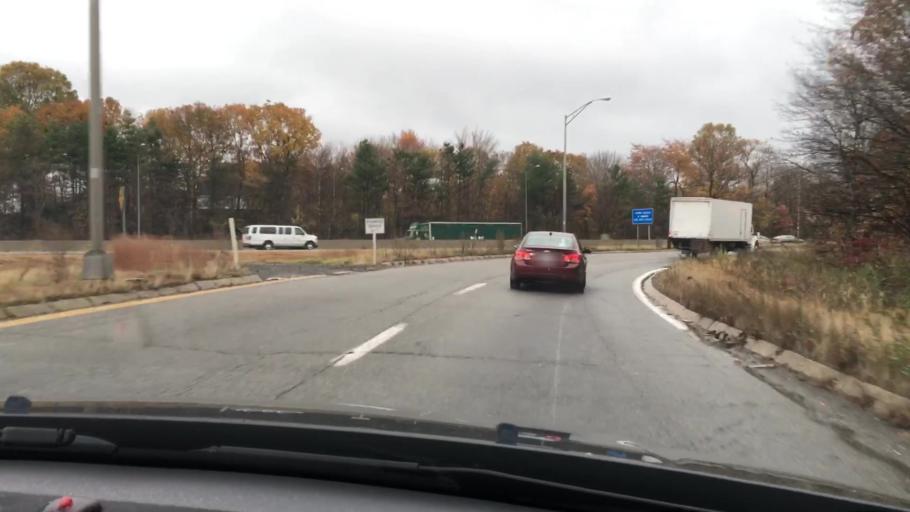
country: US
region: Massachusetts
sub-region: Worcester County
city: Westborough
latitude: 42.2639
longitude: -71.5727
